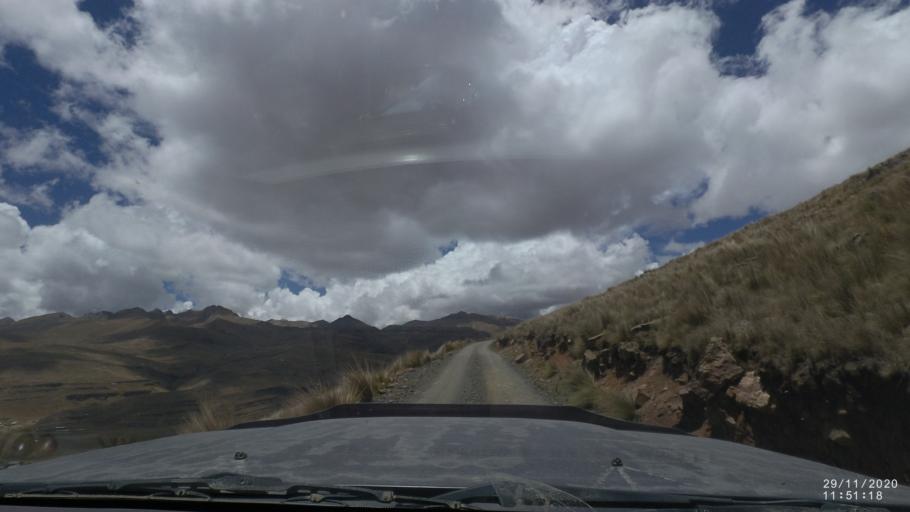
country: BO
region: Cochabamba
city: Cochabamba
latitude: -17.1717
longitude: -66.2603
